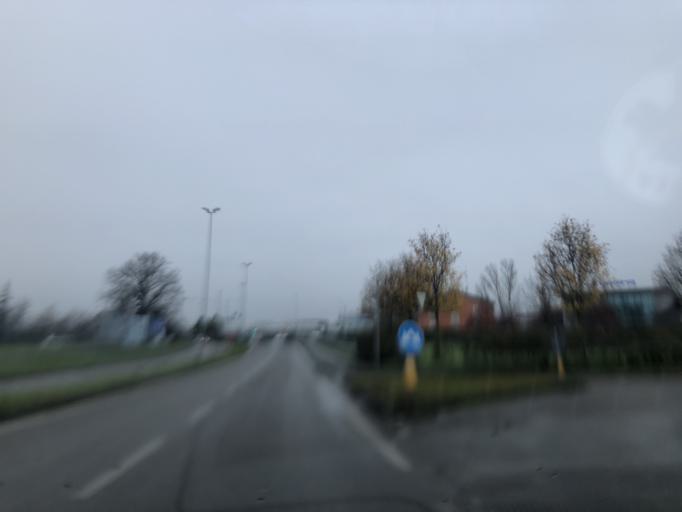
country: IT
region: Emilia-Romagna
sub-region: Provincia di Modena
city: Modena
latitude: 44.6584
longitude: 10.8834
